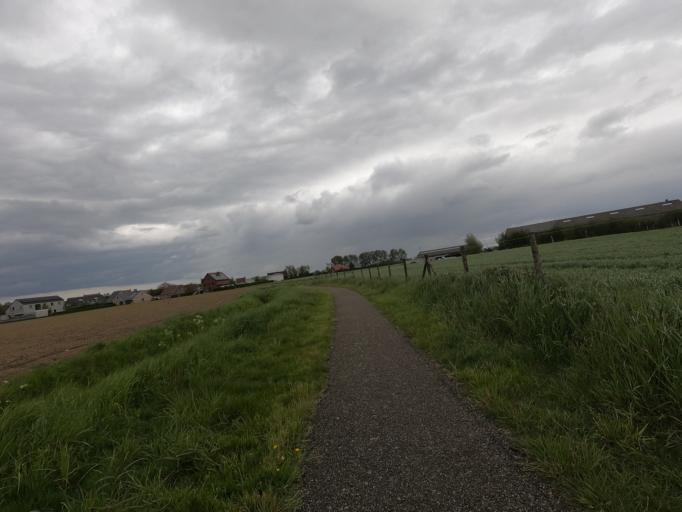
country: BE
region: Flanders
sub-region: Provincie West-Vlaanderen
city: Poperinge
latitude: 50.9303
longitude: 2.7444
